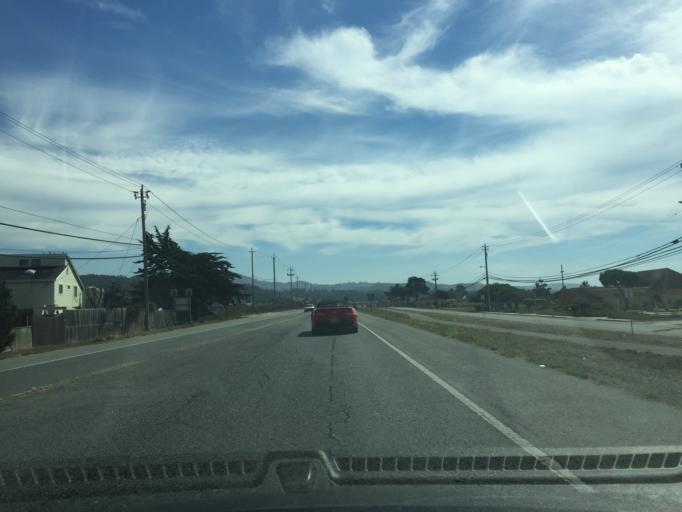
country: US
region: California
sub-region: San Mateo County
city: Half Moon Bay
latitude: 37.4756
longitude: -122.4388
